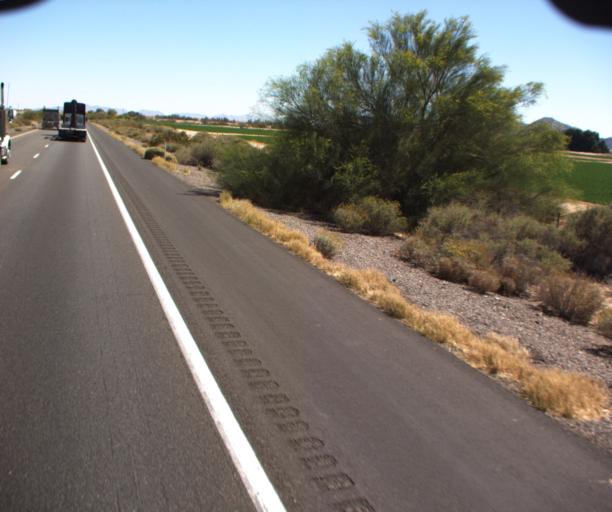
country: US
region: Arizona
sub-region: Yuma County
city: Wellton
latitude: 32.6750
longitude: -114.0646
